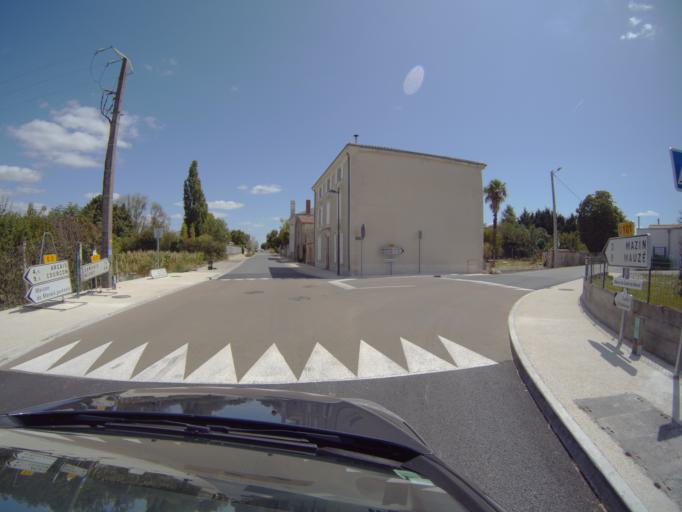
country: FR
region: Poitou-Charentes
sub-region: Departement des Deux-Sevres
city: Saint-Hilaire-la-Palud
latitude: 46.2617
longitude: -0.7107
